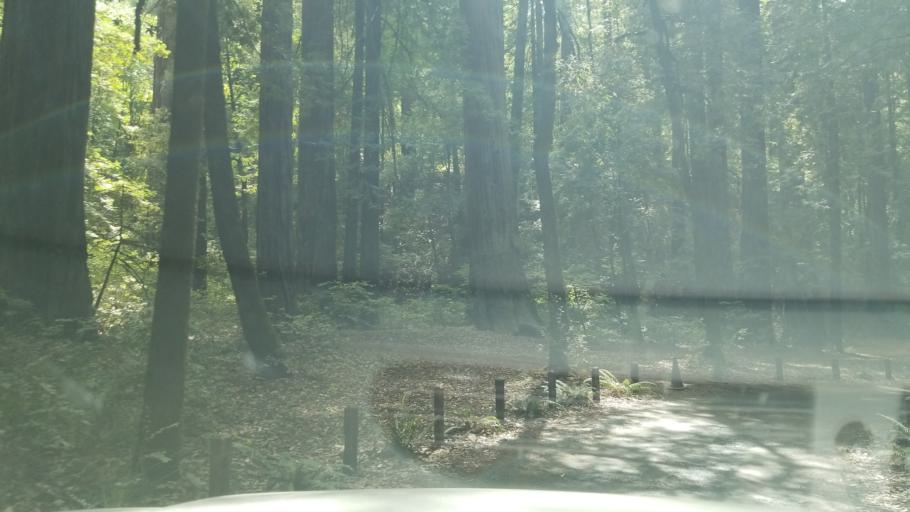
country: US
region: California
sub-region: Humboldt County
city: Redway
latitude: 39.8585
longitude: -123.7163
